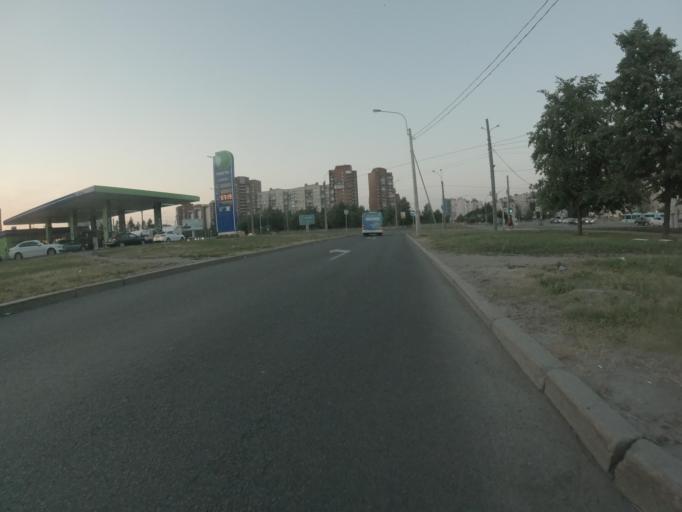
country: RU
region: St.-Petersburg
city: Krasnogvargeisky
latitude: 59.9201
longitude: 30.4696
